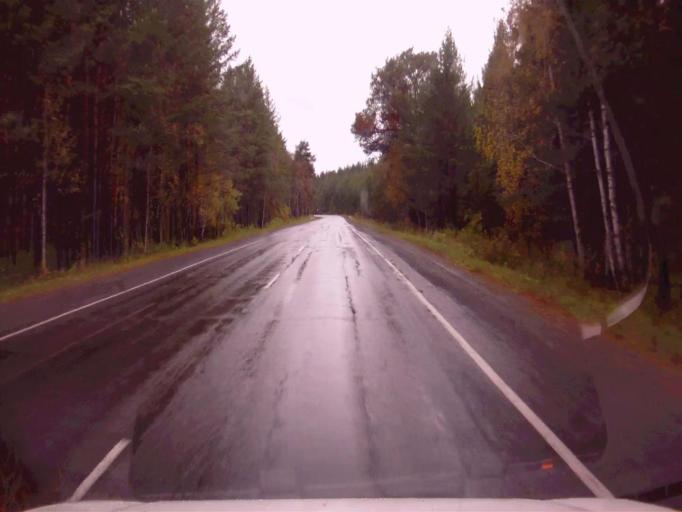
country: RU
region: Chelyabinsk
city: Verkhniy Ufaley
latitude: 56.0220
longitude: 60.3007
